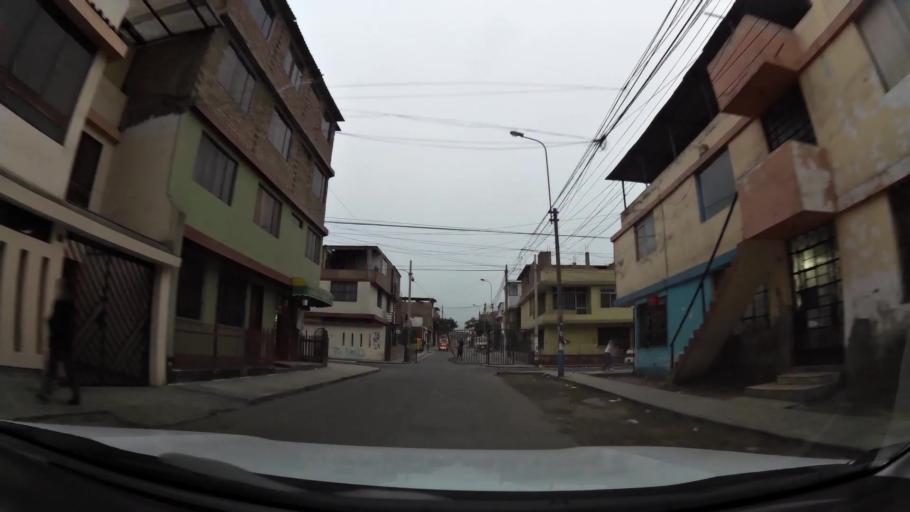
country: PE
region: Lima
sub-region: Lima
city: Surco
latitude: -12.1672
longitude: -76.9712
